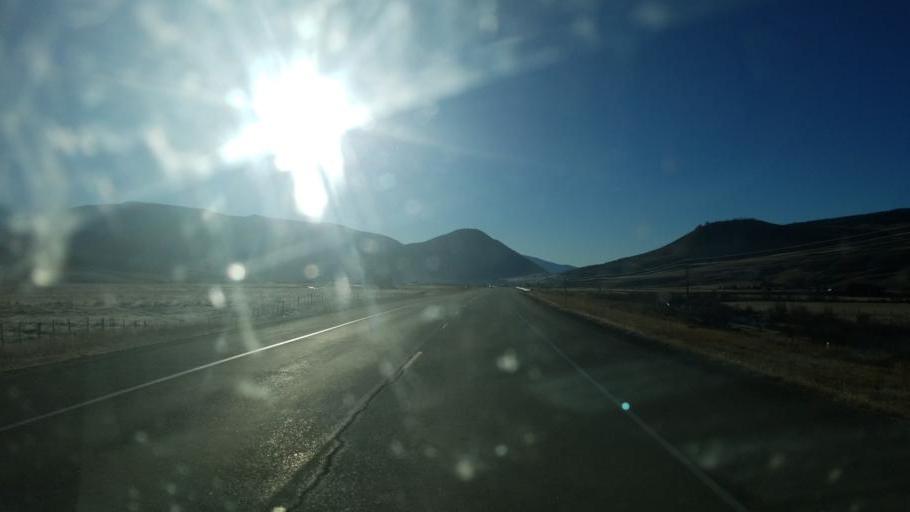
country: US
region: Colorado
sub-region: Gunnison County
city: Crested Butte
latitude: 38.8361
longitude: -106.9329
